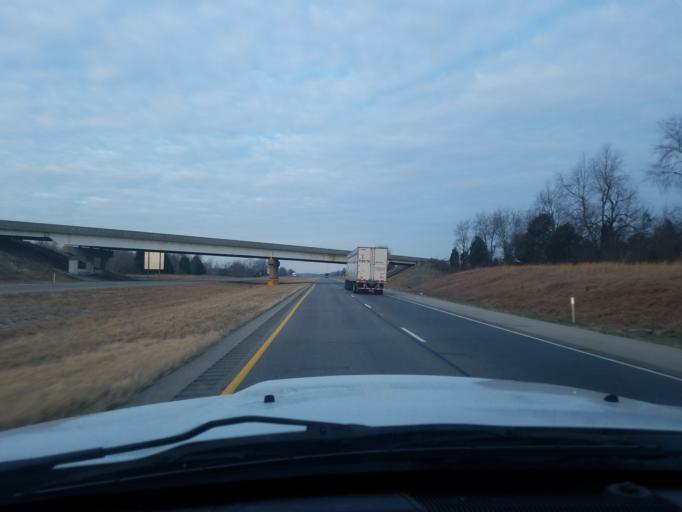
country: US
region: Indiana
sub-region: Harrison County
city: Corydon
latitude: 38.2402
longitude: -86.1531
